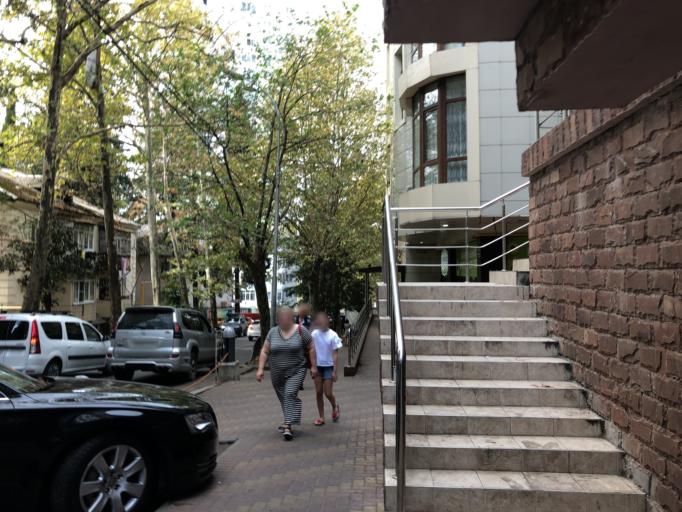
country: RU
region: Krasnodarskiy
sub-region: Sochi City
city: Sochi
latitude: 43.5935
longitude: 39.7370
